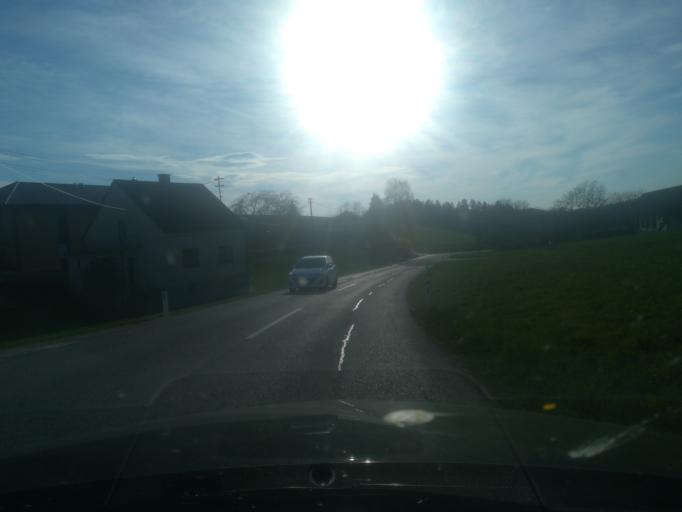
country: AT
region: Upper Austria
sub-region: Politischer Bezirk Perg
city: Bad Kreuzen
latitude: 48.2624
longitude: 14.8050
